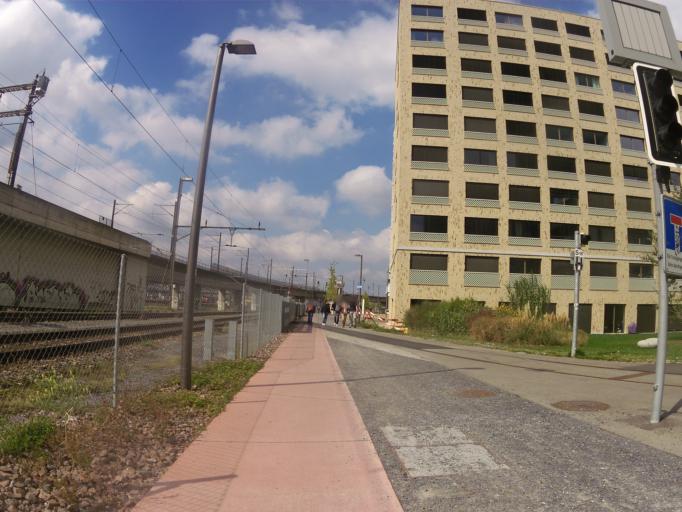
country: CH
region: Zurich
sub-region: Bezirk Zuerich
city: Zuerich (Kreis 5) / Escher-Wyss
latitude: 47.3860
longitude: 8.5149
